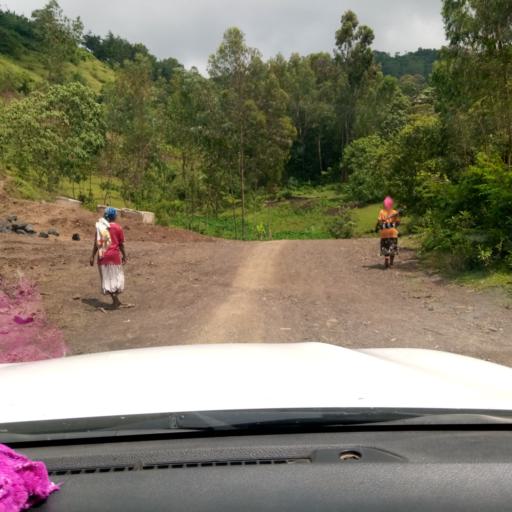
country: ET
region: Southern Nations, Nationalities, and People's Region
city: Arba Minch'
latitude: 6.3133
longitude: 37.3697
